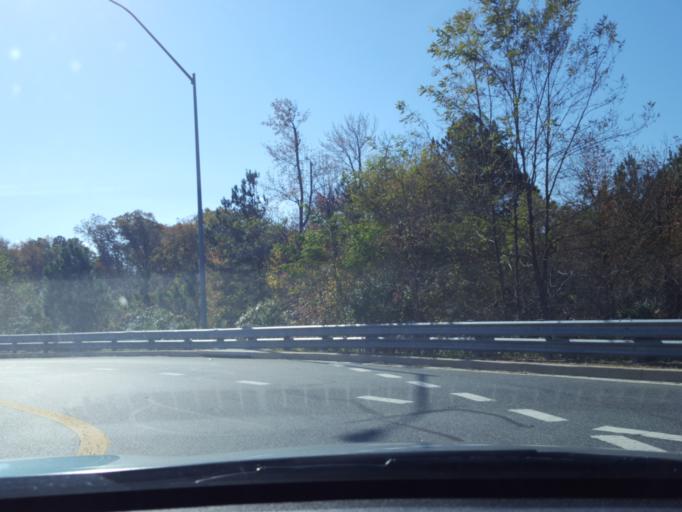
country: US
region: Maryland
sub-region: Calvert County
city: Chesapeake Ranch Estates
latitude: 38.3643
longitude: -76.4496
